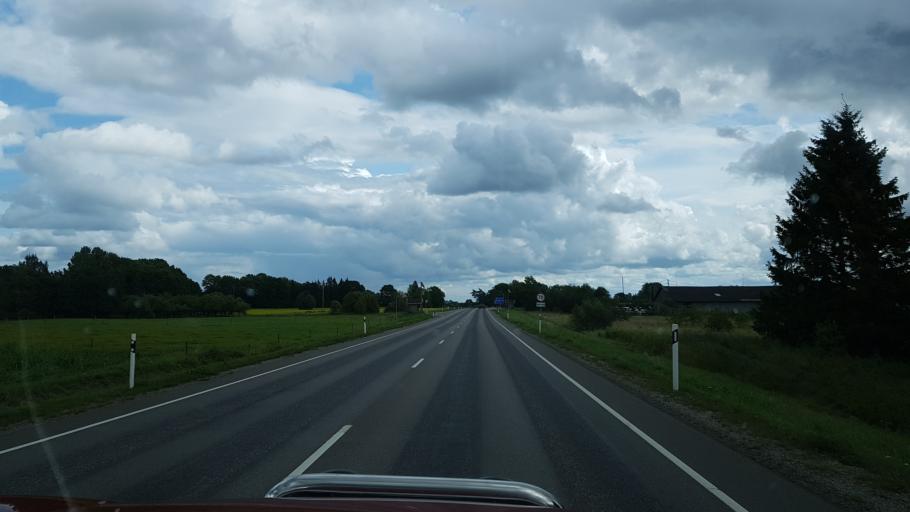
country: EE
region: Laeaene
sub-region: Lihula vald
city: Lihula
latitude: 58.7245
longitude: 23.9205
